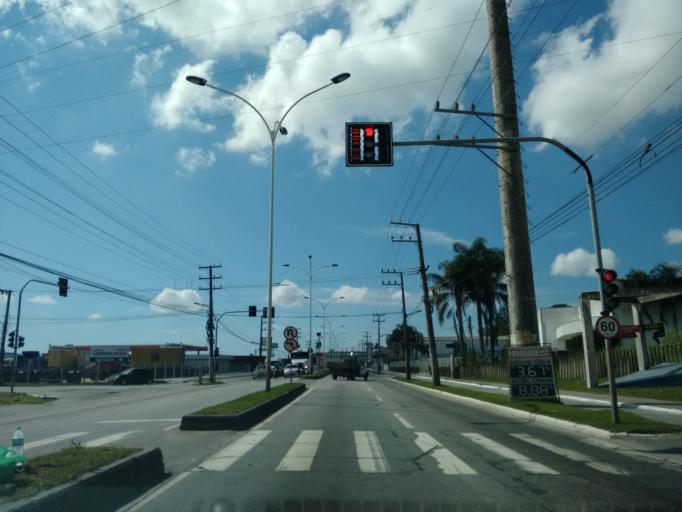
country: BR
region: Santa Catarina
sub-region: Itajai
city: Itajai
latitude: -26.8913
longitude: -48.7141
